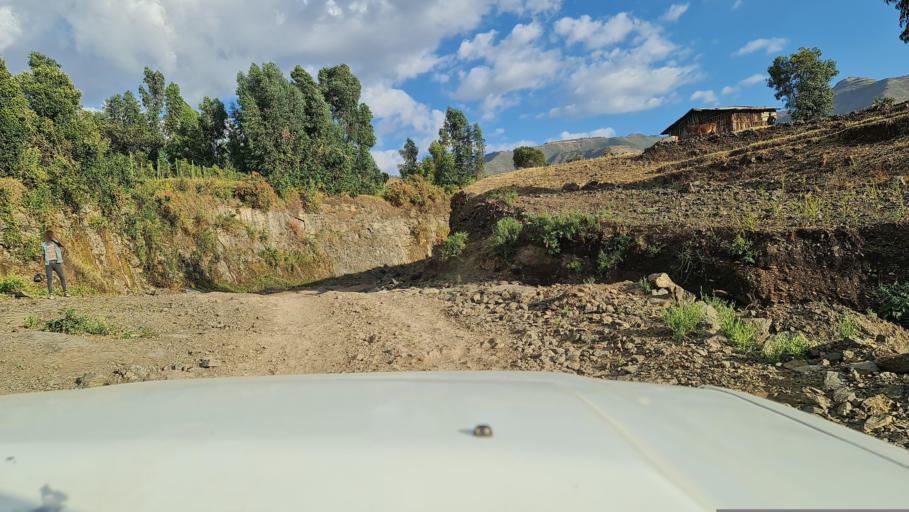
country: ET
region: Amhara
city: Debark'
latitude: 13.0411
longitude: 38.0379
